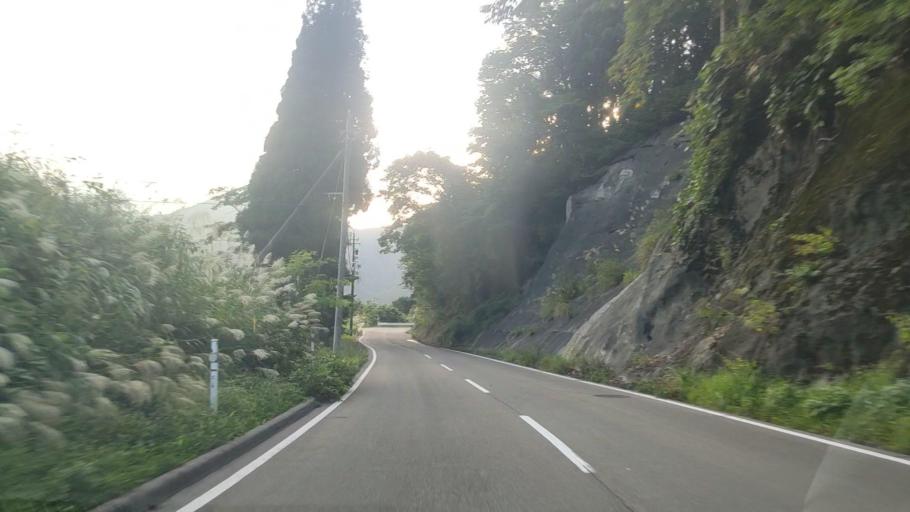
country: JP
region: Toyama
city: Yatsuomachi-higashikumisaka
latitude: 36.4798
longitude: 137.0324
